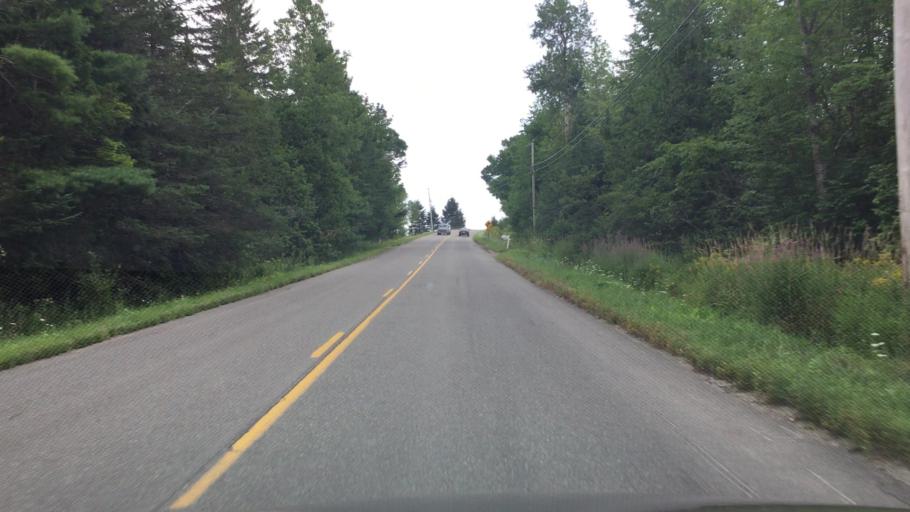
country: US
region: Maine
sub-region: Waldo County
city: Winterport
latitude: 44.6826
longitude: -68.8694
